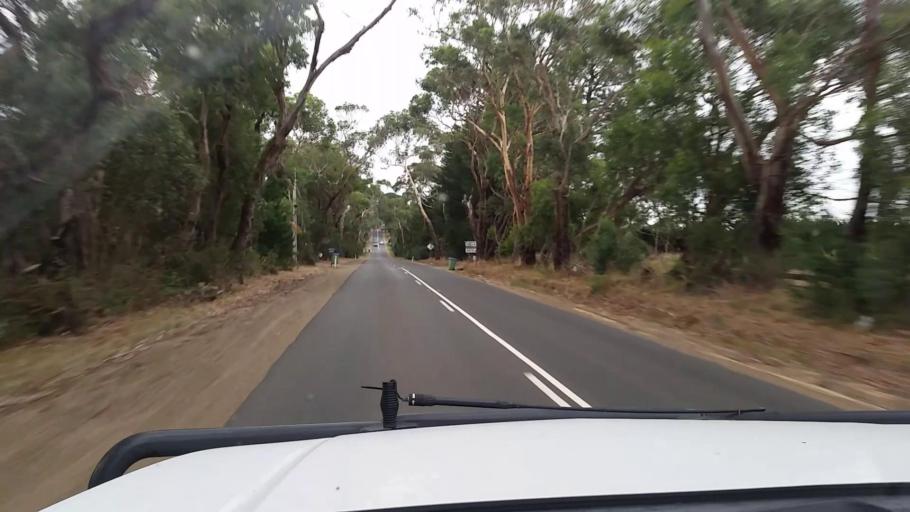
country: AU
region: Victoria
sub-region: Mornington Peninsula
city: Hastings
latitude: -38.3166
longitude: 145.1457
